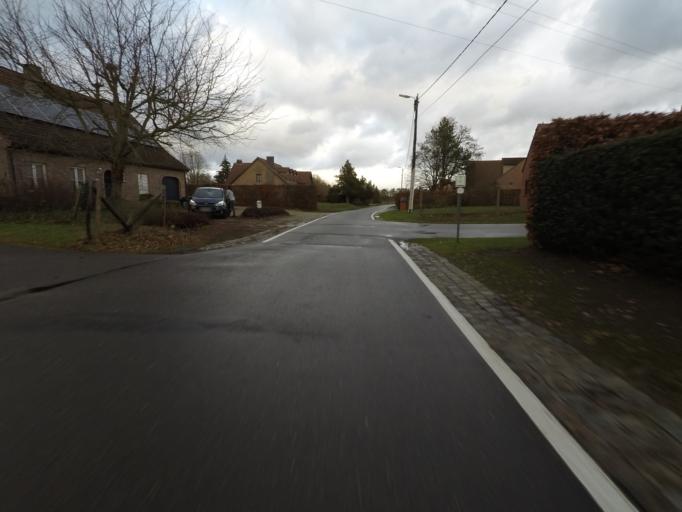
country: BE
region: Flanders
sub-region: Provincie Vlaams-Brabant
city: Begijnendijk
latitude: 51.0126
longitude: 4.7714
